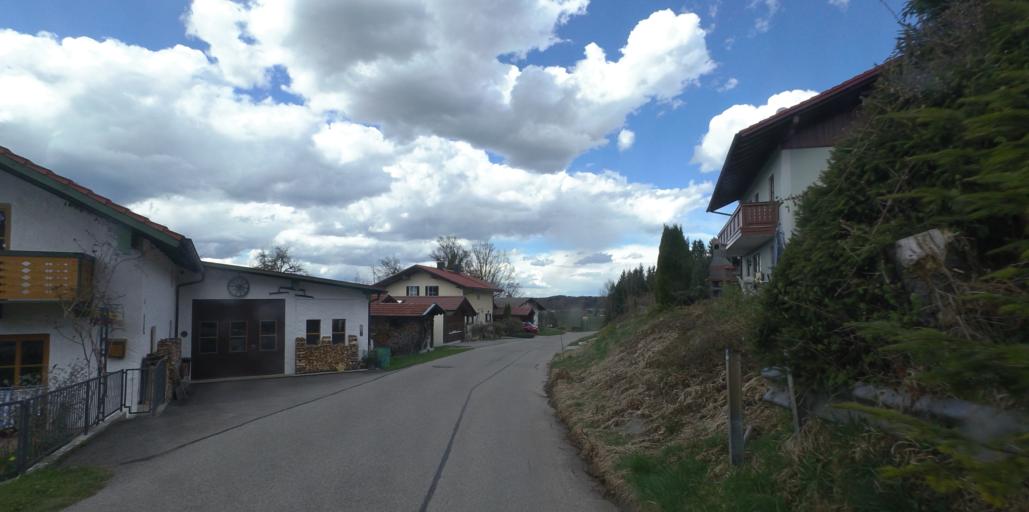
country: DE
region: Bavaria
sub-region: Upper Bavaria
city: Vachendorf
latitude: 47.8316
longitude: 12.6034
